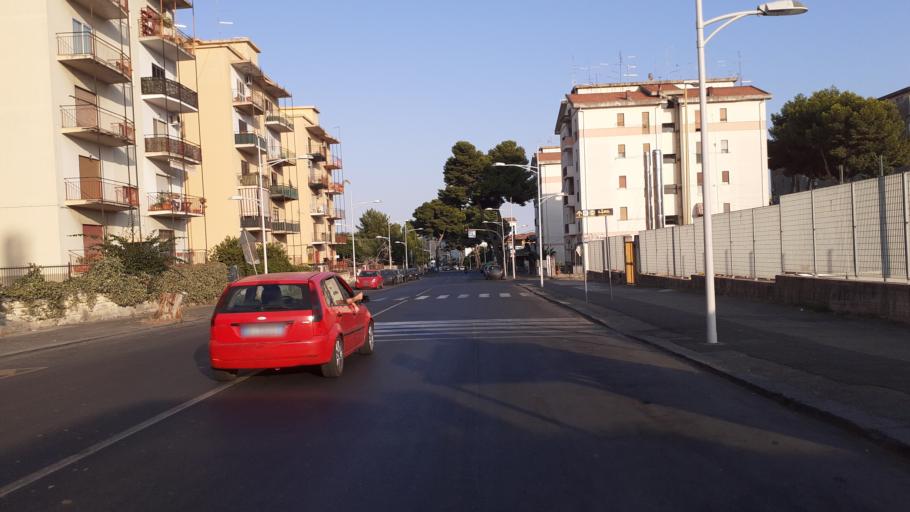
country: IT
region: Sicily
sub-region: Catania
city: Catania
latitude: 37.5039
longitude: 15.0567
